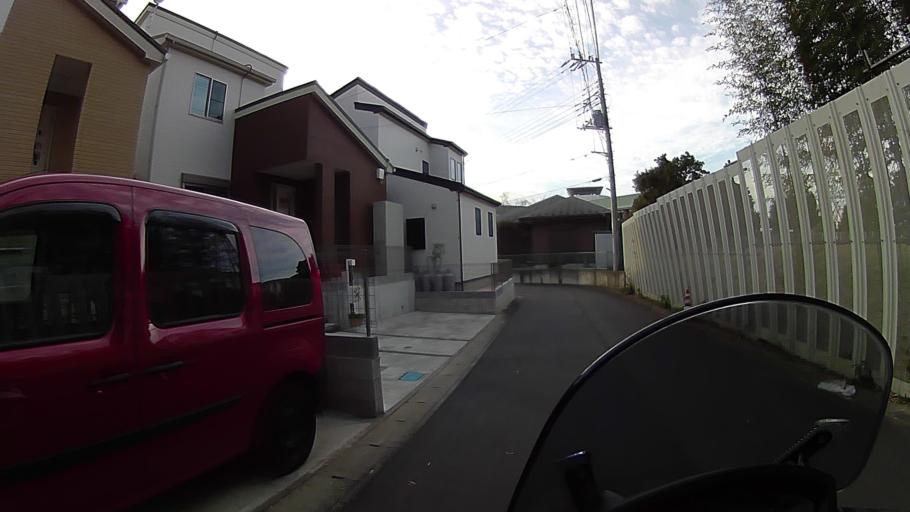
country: JP
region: Kanagawa
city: Atsugi
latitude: 35.4203
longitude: 139.4227
